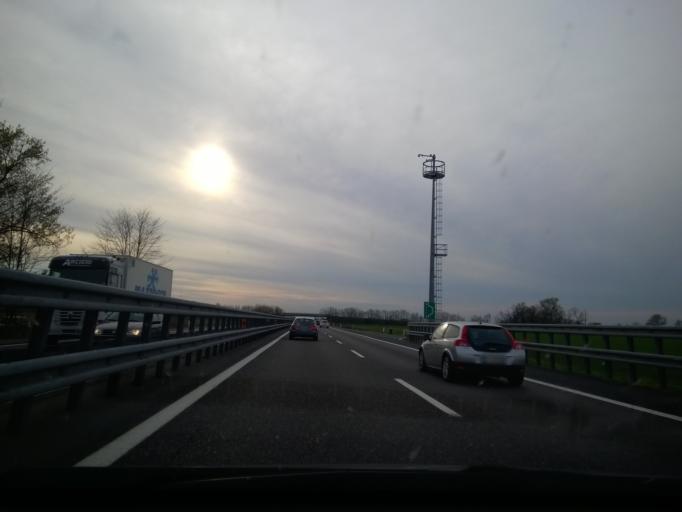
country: IT
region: Emilia-Romagna
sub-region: Provincia di Piacenza
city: Rottofreno
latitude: 45.0648
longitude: 9.5679
